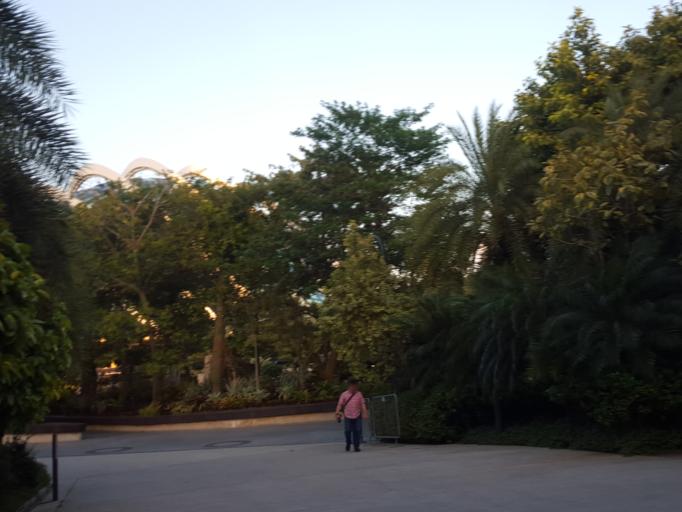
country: SG
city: Singapore
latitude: 1.2834
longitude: 103.8645
